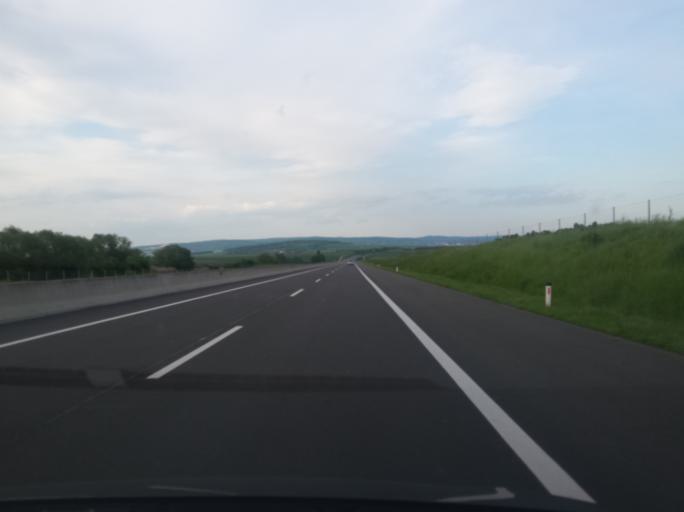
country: AT
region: Burgenland
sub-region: Politischer Bezirk Mattersburg
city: Krensdorf
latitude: 47.7773
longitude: 16.4339
